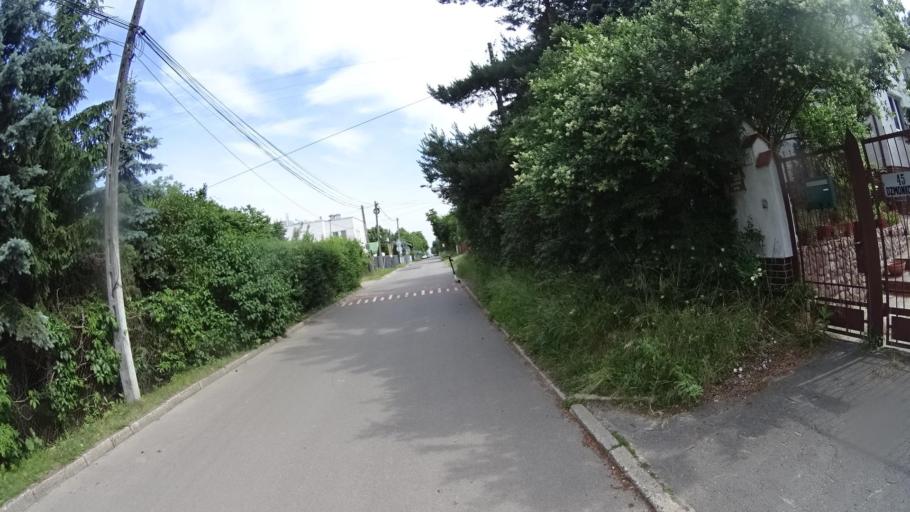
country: PL
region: Masovian Voivodeship
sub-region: Powiat pruszkowski
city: Raszyn
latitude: 52.1729
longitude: 20.9258
